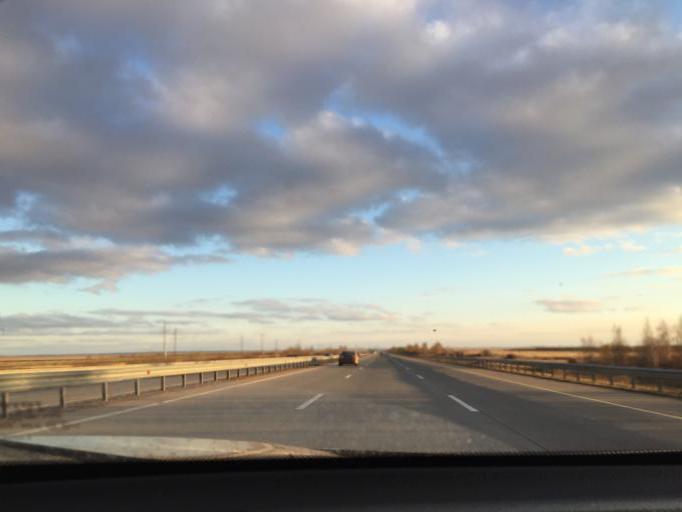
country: KZ
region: Astana Qalasy
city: Astana
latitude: 51.3369
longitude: 71.3417
